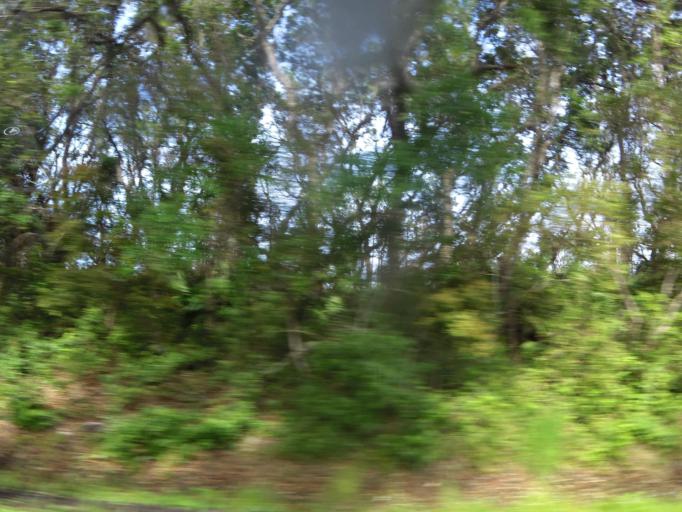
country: US
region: Florida
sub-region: Nassau County
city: Fernandina Beach
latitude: 30.5000
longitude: -81.4726
